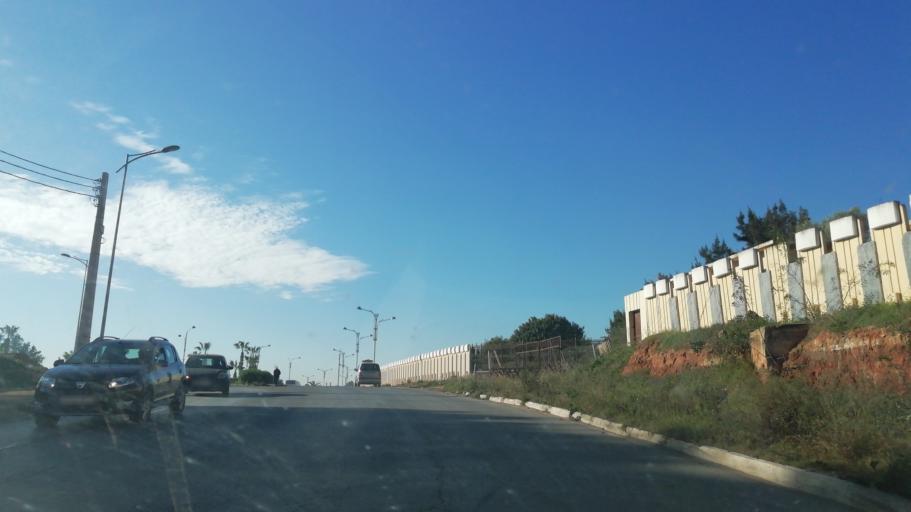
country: DZ
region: Oran
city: Oran
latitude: 35.6851
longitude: -0.6704
